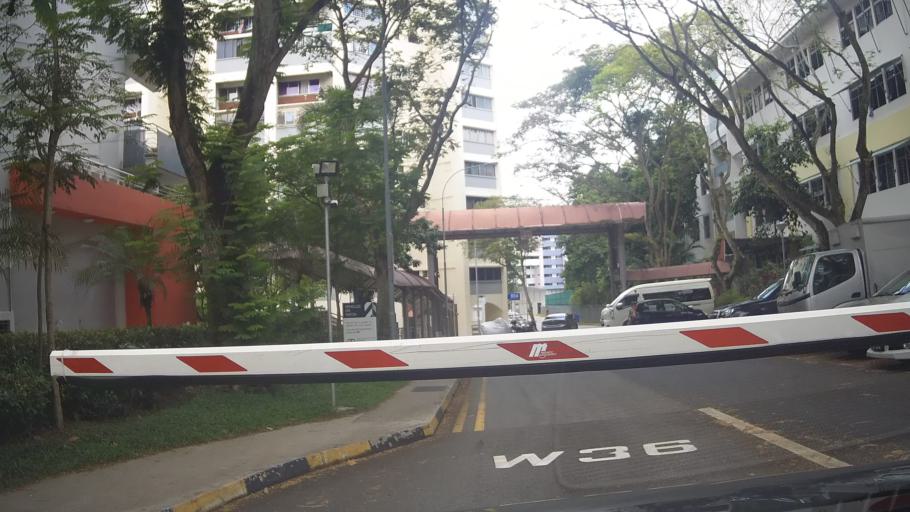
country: MY
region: Johor
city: Johor Bahru
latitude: 1.4399
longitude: 103.7886
